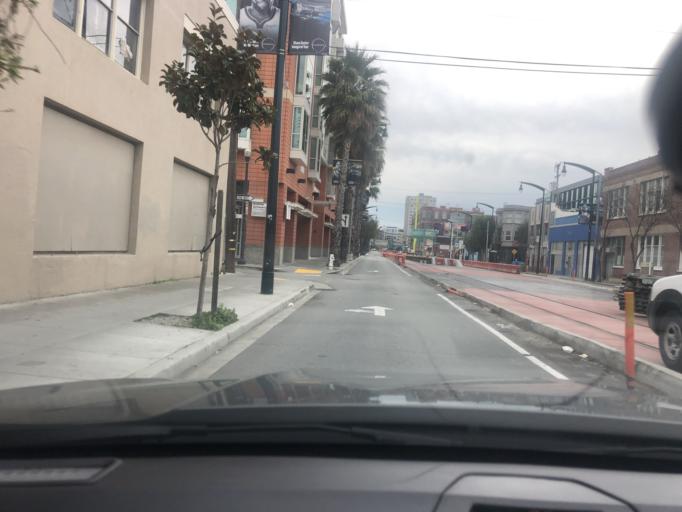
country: US
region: California
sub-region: San Francisco County
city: San Francisco
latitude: 37.7794
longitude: -122.3977
